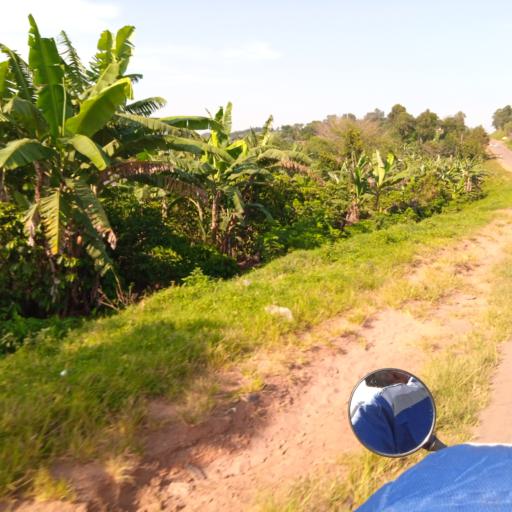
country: UG
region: Central Region
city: Masaka
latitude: -0.4194
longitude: 31.6738
